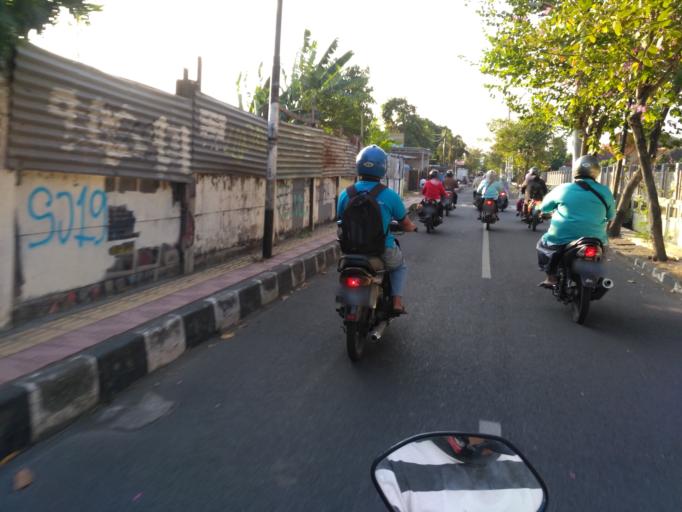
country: ID
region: Daerah Istimewa Yogyakarta
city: Yogyakarta
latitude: -7.8148
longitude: 110.3834
